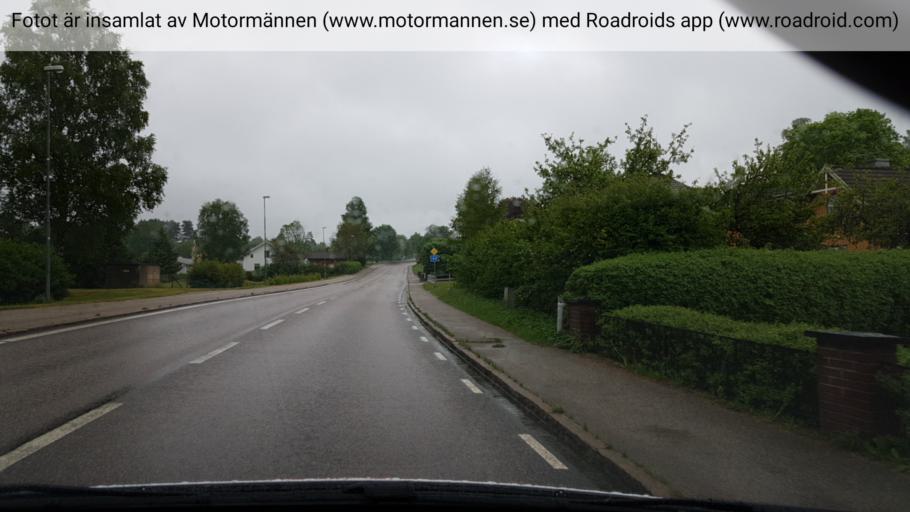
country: SE
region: Vaestra Goetaland
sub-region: Ulricehamns Kommun
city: Ulricehamn
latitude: 57.9312
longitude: 13.4947
